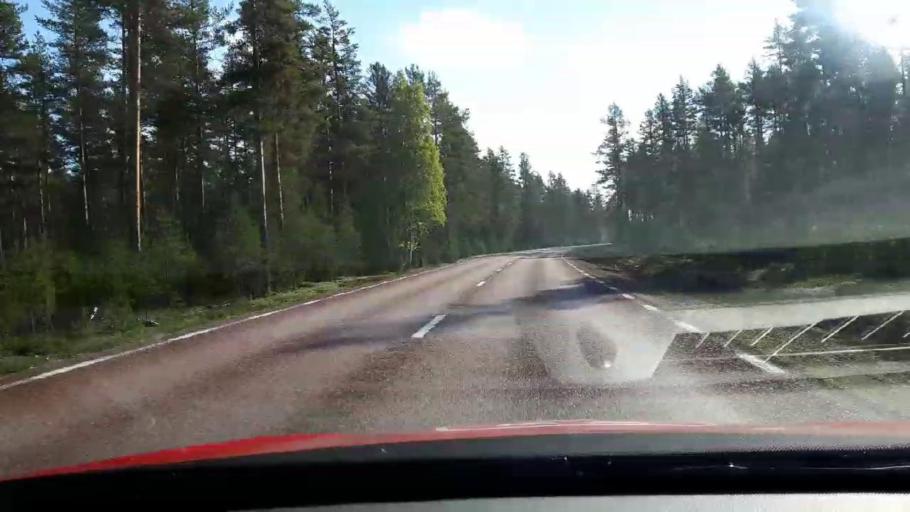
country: SE
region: Gaevleborg
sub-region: Ljusdals Kommun
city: Farila
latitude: 61.9200
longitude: 15.6109
